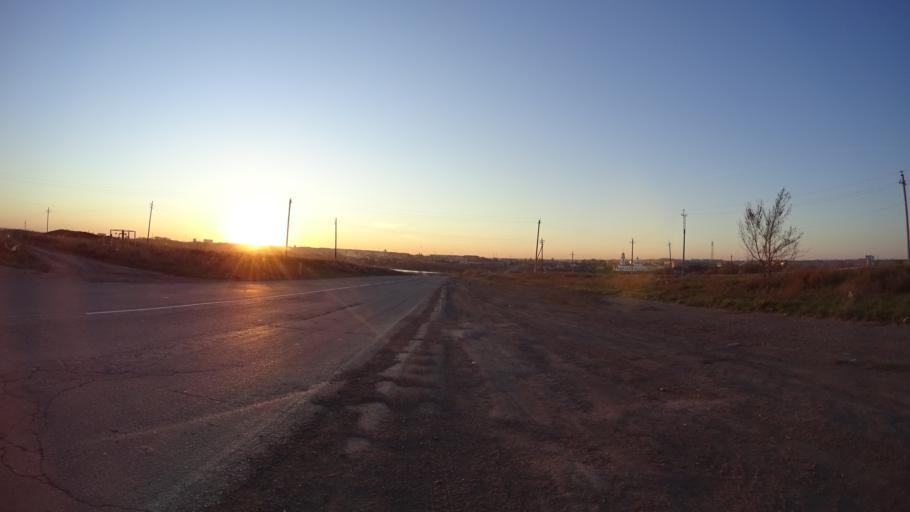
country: RU
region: Chelyabinsk
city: Troitsk
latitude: 54.0714
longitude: 61.5603
